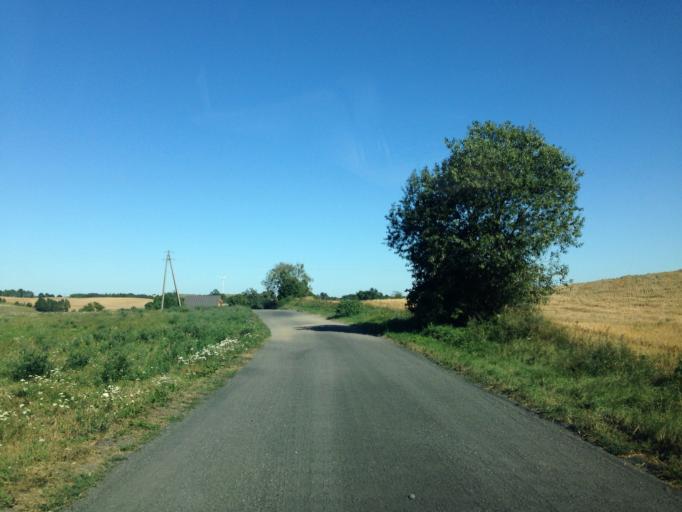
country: PL
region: Kujawsko-Pomorskie
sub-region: Powiat brodnicki
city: Brodnica
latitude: 53.2113
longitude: 19.4543
